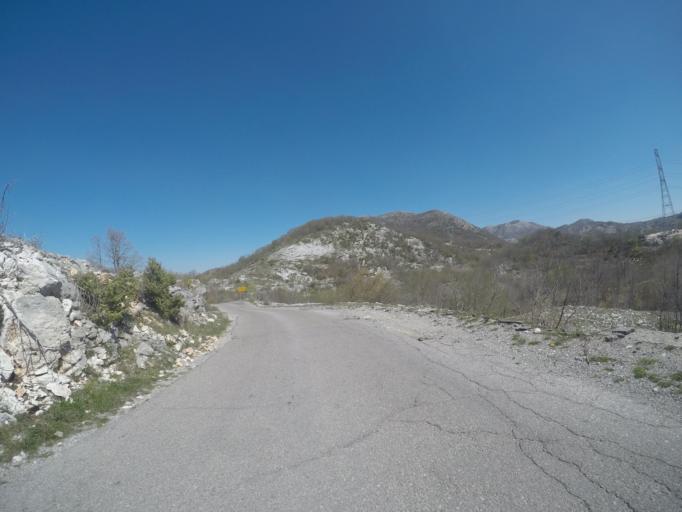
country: ME
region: Cetinje
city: Cetinje
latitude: 42.4412
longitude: 18.8746
